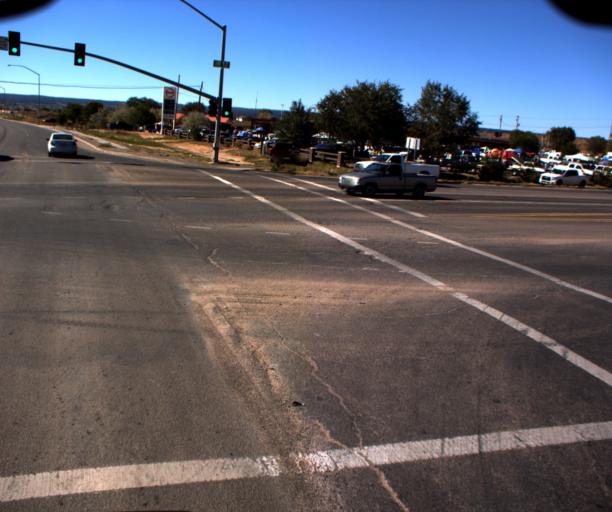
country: US
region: Arizona
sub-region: Apache County
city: Window Rock
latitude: 35.6635
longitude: -109.0569
